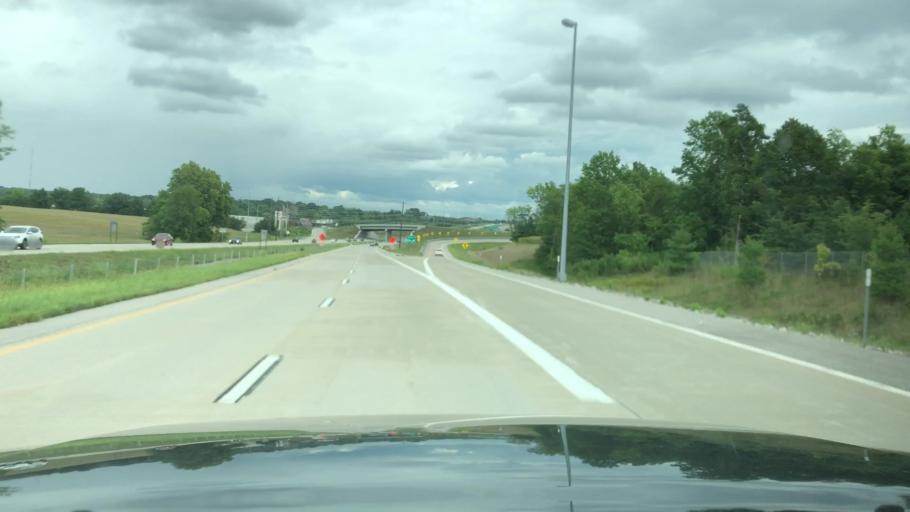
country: US
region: Missouri
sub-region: Saint Charles County
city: Cottleville
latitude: 38.7349
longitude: -90.6422
